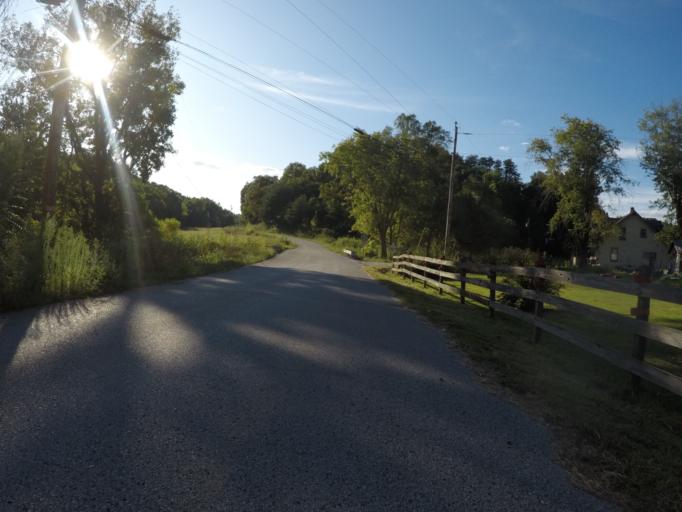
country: US
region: West Virginia
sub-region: Cabell County
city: Huntington
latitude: 38.5213
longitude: -82.5027
